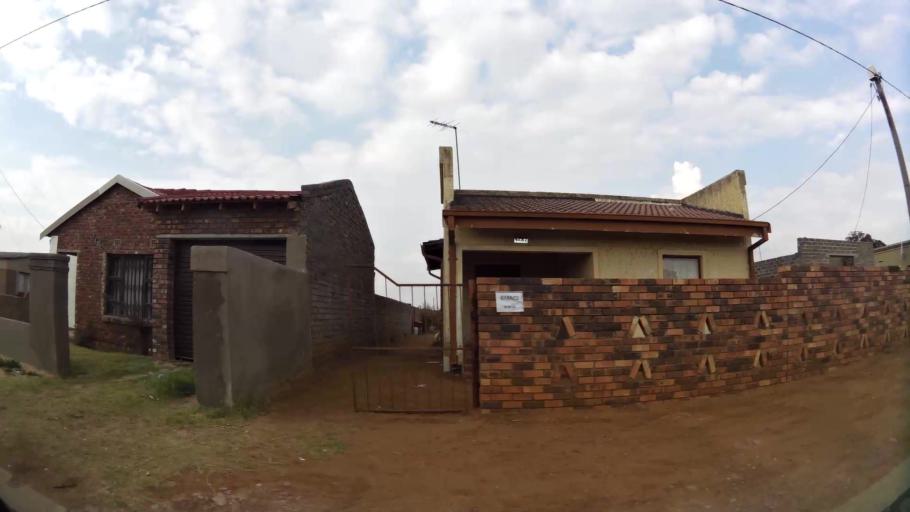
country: ZA
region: Gauteng
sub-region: Sedibeng District Municipality
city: Vanderbijlpark
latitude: -26.6769
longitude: 27.8586
